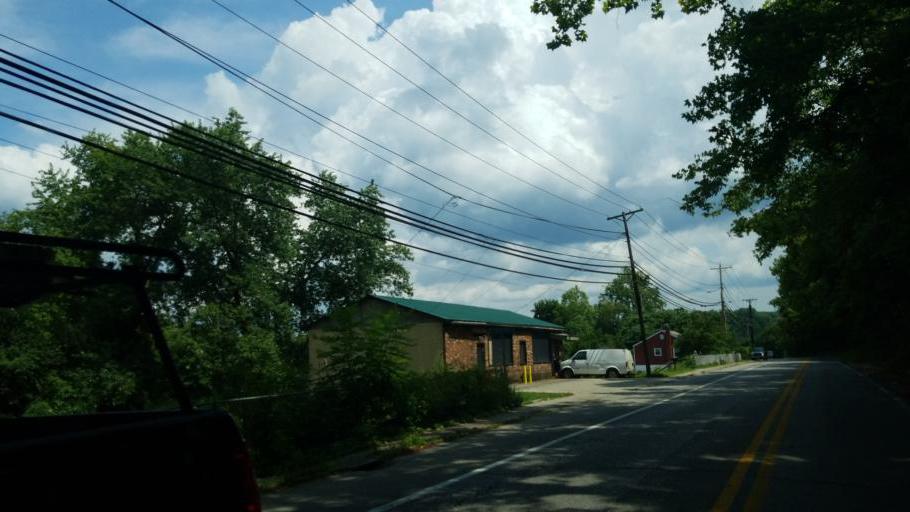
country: US
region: West Virginia
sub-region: Kanawha County
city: Saint Albans
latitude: 38.3890
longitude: -81.8457
